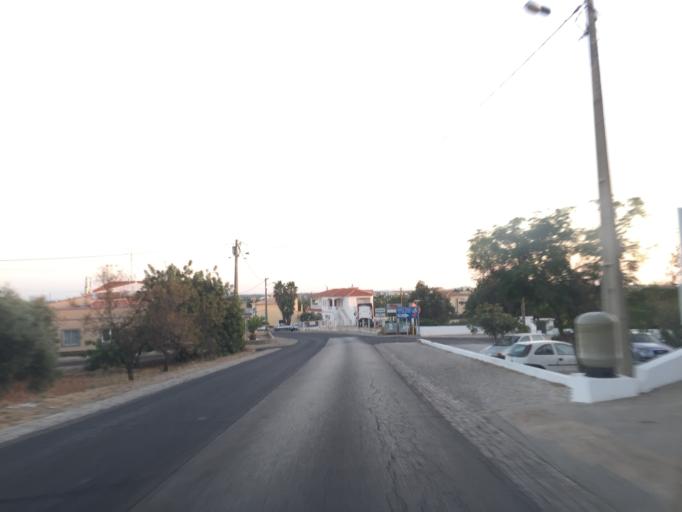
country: PT
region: Faro
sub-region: Loule
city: Almancil
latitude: 37.0977
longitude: -8.0242
